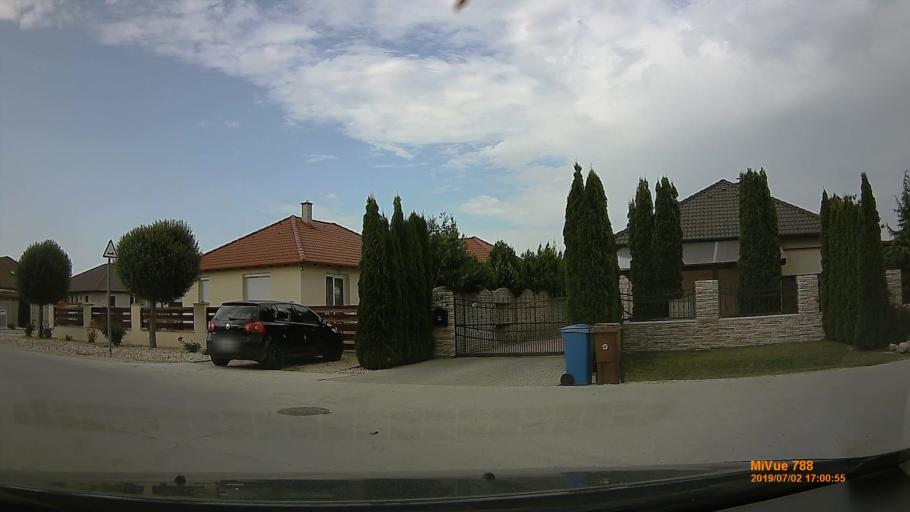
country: HU
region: Gyor-Moson-Sopron
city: Halaszi
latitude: 47.8892
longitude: 17.2941
